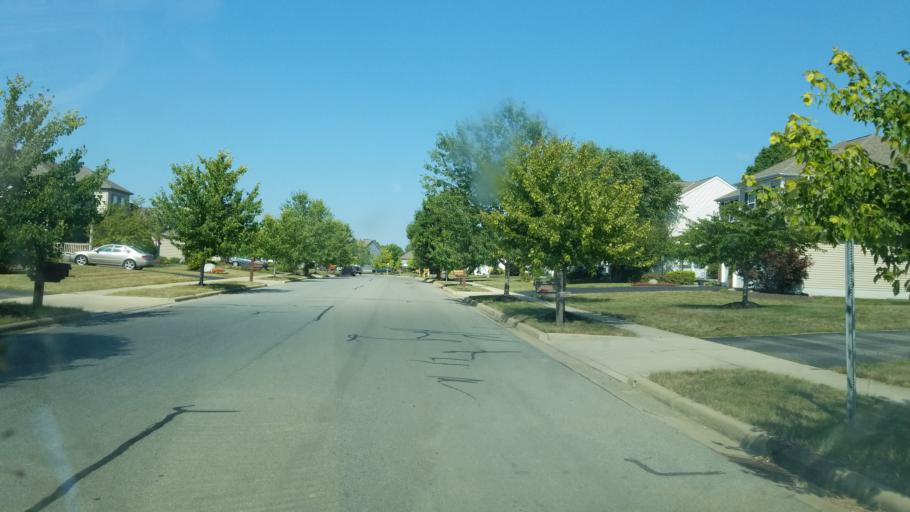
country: US
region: Ohio
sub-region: Delaware County
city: Sunbury
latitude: 40.2340
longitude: -82.9351
